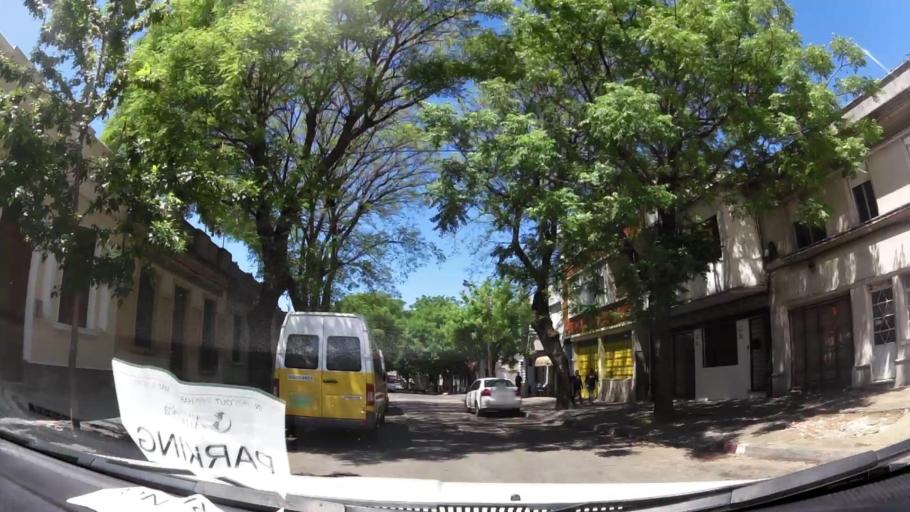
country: UY
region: Montevideo
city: Montevideo
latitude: -34.8881
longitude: -56.1708
